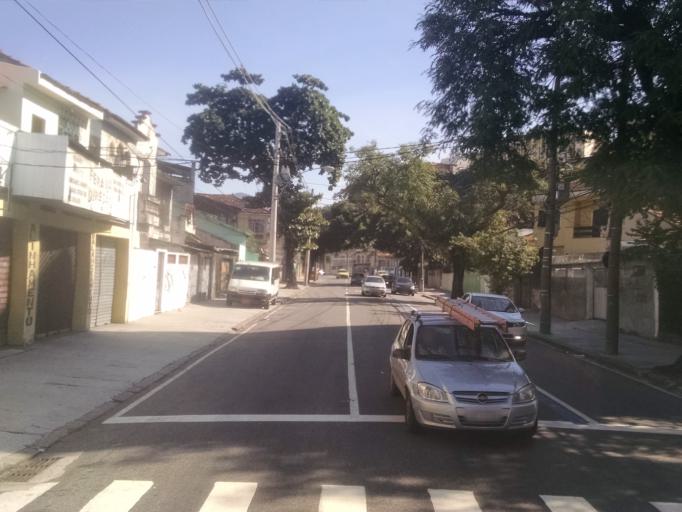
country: BR
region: Rio de Janeiro
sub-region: Rio De Janeiro
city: Rio de Janeiro
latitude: -22.9080
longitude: -43.2722
